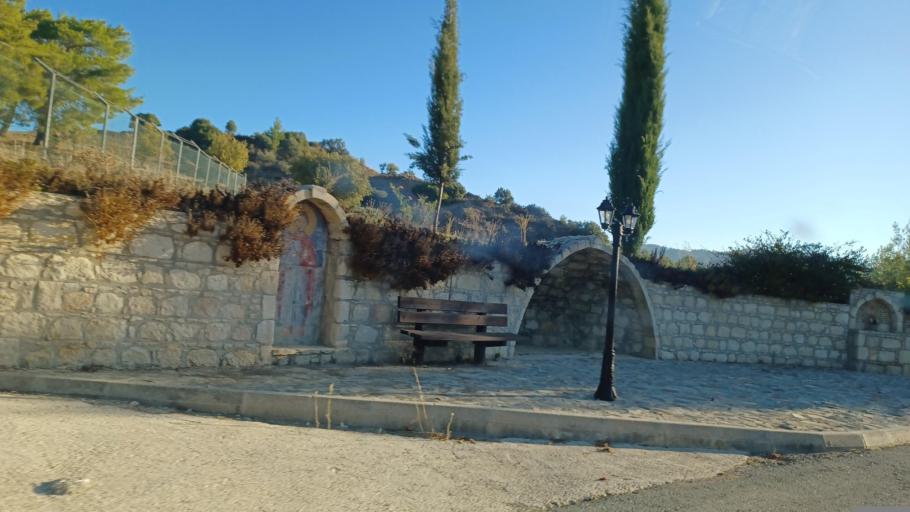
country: CY
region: Pafos
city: Polis
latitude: 34.9440
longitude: 32.5674
